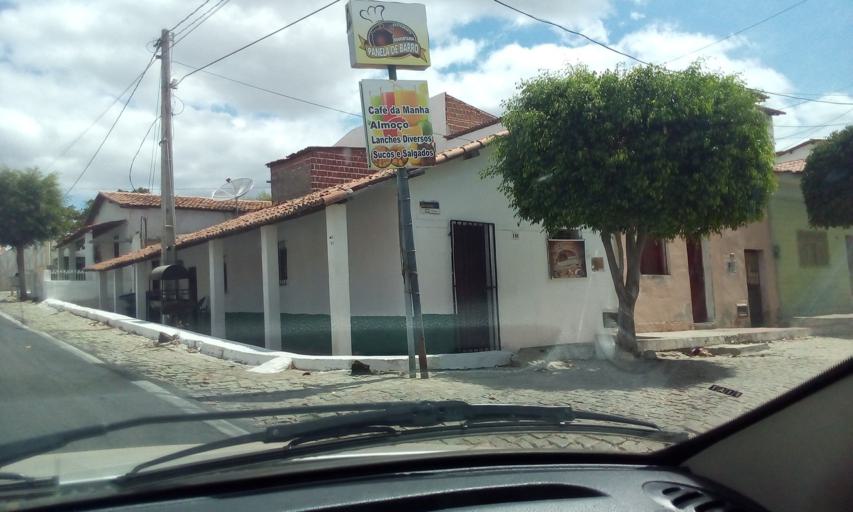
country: BR
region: Rio Grande do Norte
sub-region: Currais Novos
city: Currais Novos
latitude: -6.2638
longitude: -36.5184
